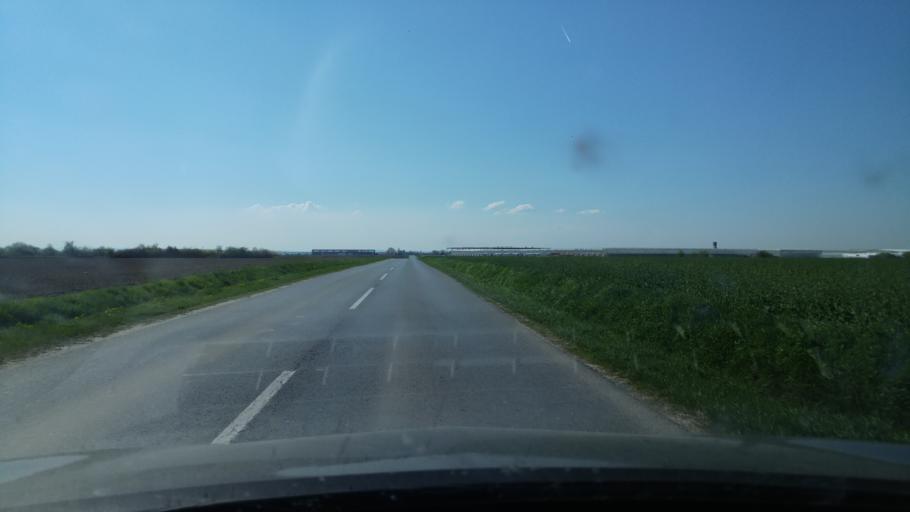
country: HR
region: Osjecko-Baranjska
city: Viskovci
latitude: 45.3447
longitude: 18.4420
